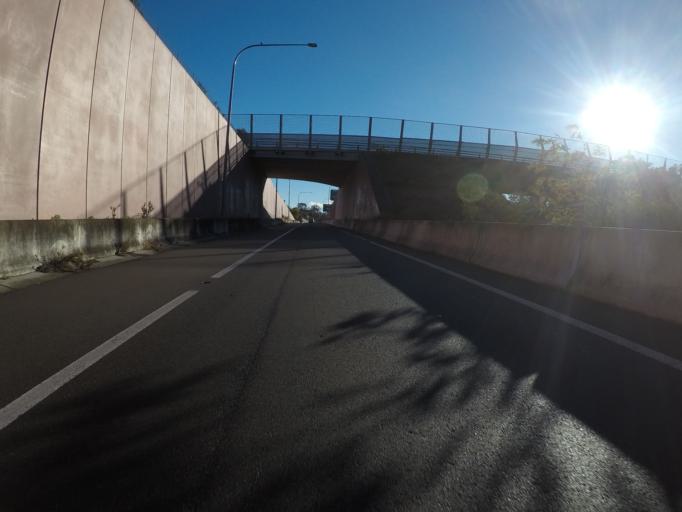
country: AU
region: Australian Capital Territory
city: Macquarie
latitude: -35.2617
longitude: 149.0865
